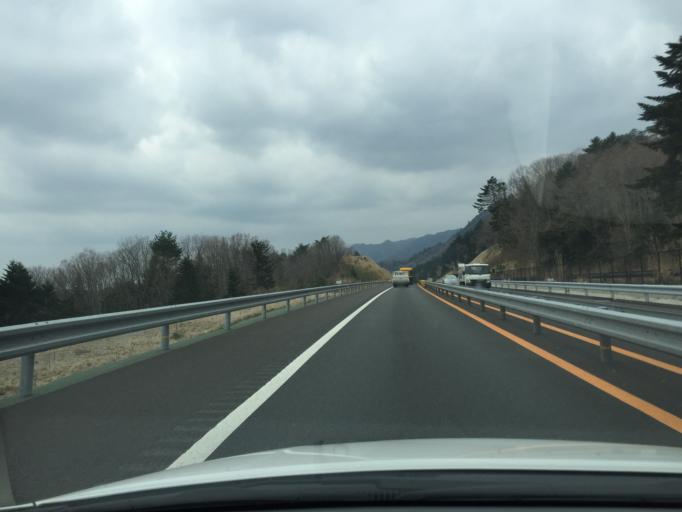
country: JP
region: Miyagi
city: Marumori
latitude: 37.8316
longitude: 140.8777
